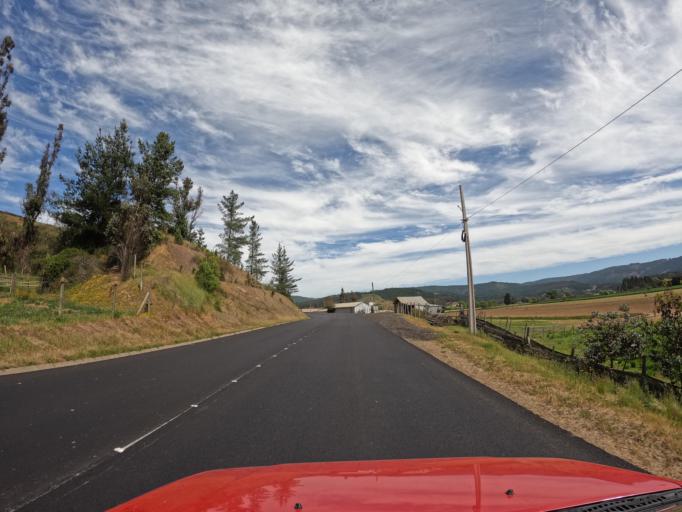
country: CL
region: Maule
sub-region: Provincia de Talca
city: Constitucion
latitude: -35.0751
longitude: -72.0393
